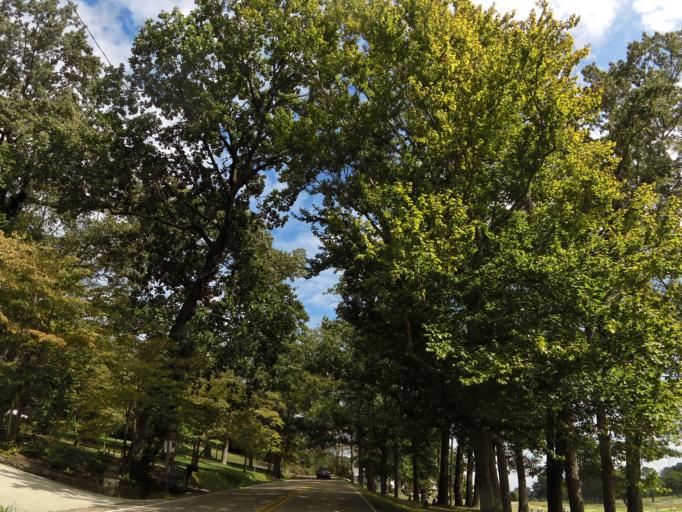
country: US
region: Tennessee
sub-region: Knox County
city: Knoxville
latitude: 35.9947
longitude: -83.8433
